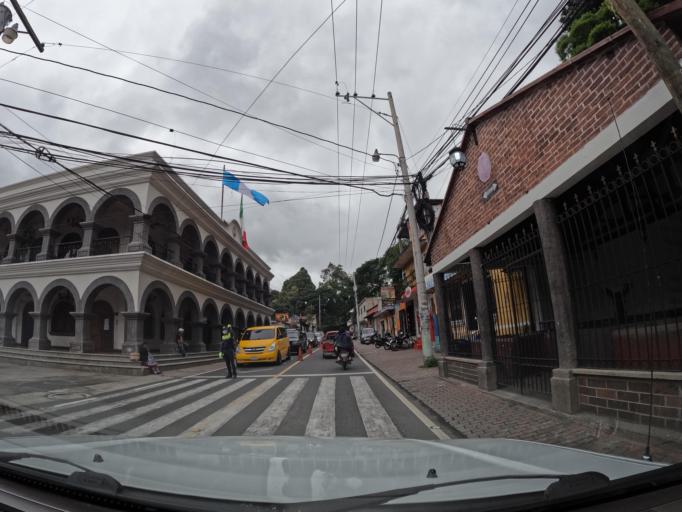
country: GT
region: Sacatepequez
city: Pastores
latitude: 14.5939
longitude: -90.7532
